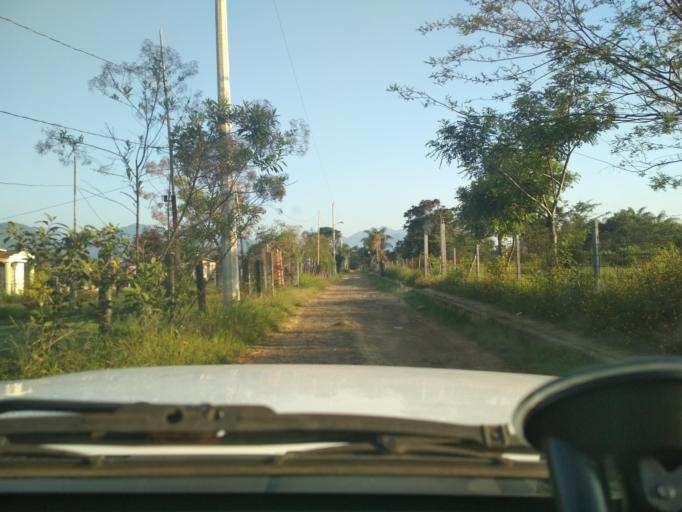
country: MX
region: Veracruz
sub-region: Fortin
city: Fraccionamiento Villas de la Llave
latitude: 18.9192
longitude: -96.9986
